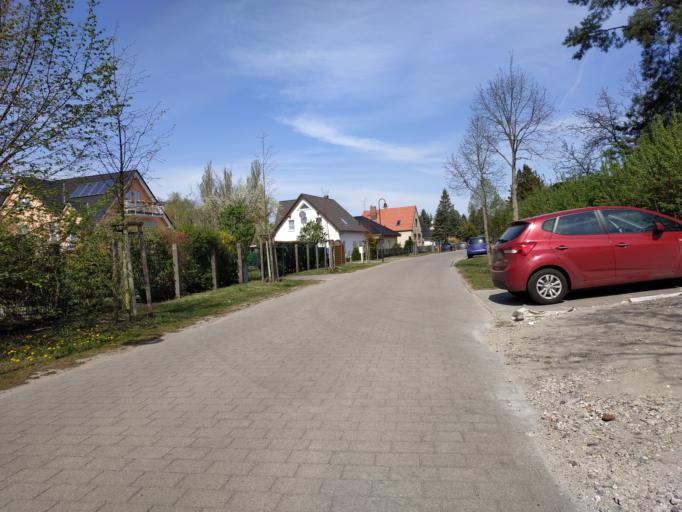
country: DE
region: Brandenburg
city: Petershagen
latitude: 52.5401
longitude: 13.8205
